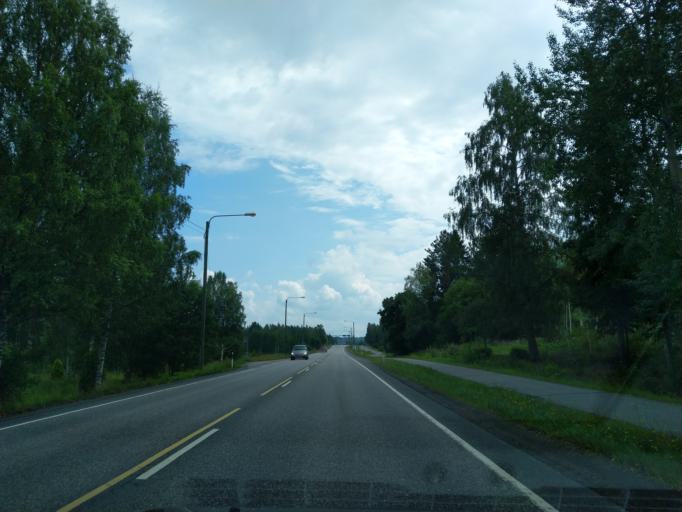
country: FI
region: South Karelia
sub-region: Imatra
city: Parikkala
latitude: 61.5907
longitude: 29.4891
